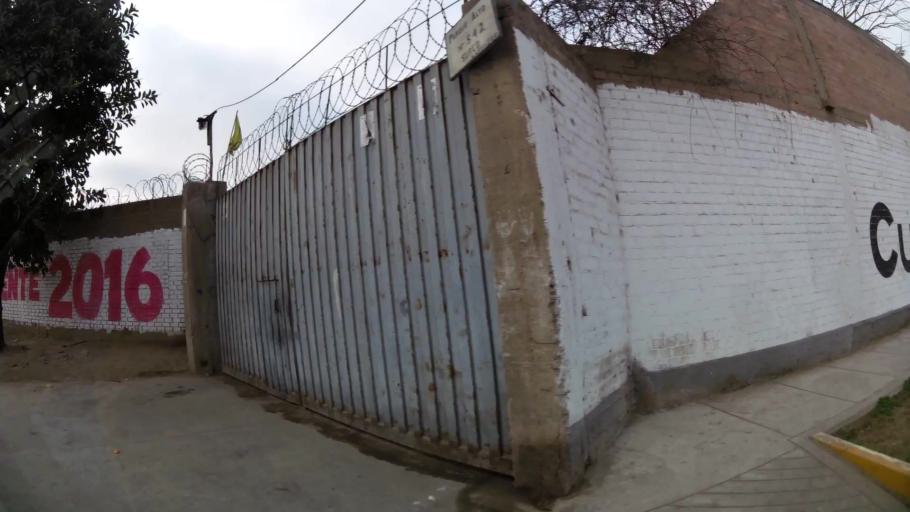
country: PE
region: Lima
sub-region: Lima
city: Surco
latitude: -12.1441
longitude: -77.0127
